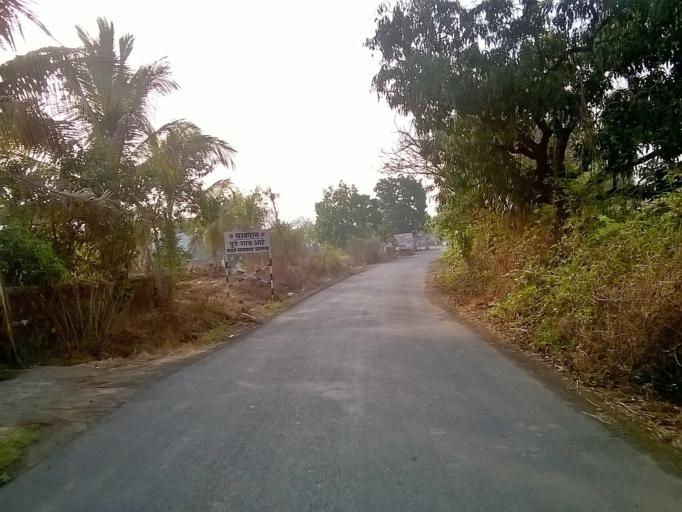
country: IN
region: Maharashtra
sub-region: Raigarh
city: Kalundri
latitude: 19.0185
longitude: 73.1899
